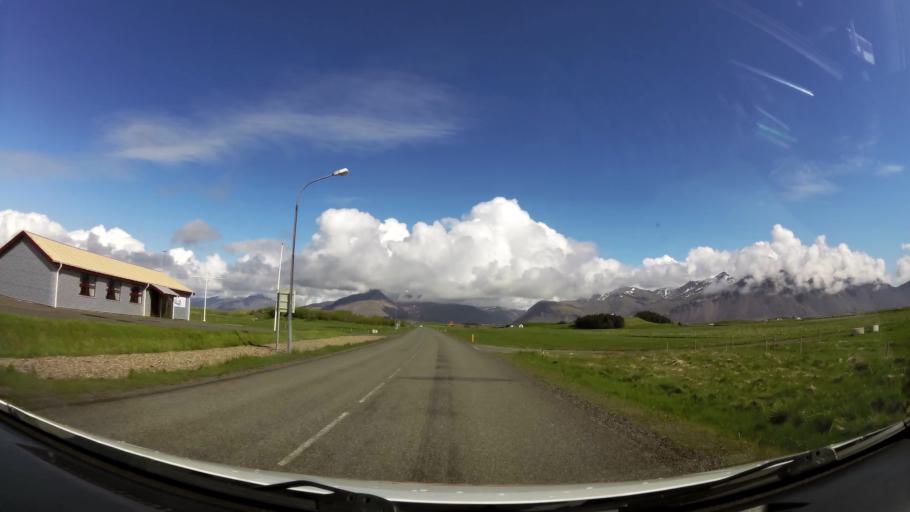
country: IS
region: East
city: Hoefn
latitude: 64.2637
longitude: -15.2019
